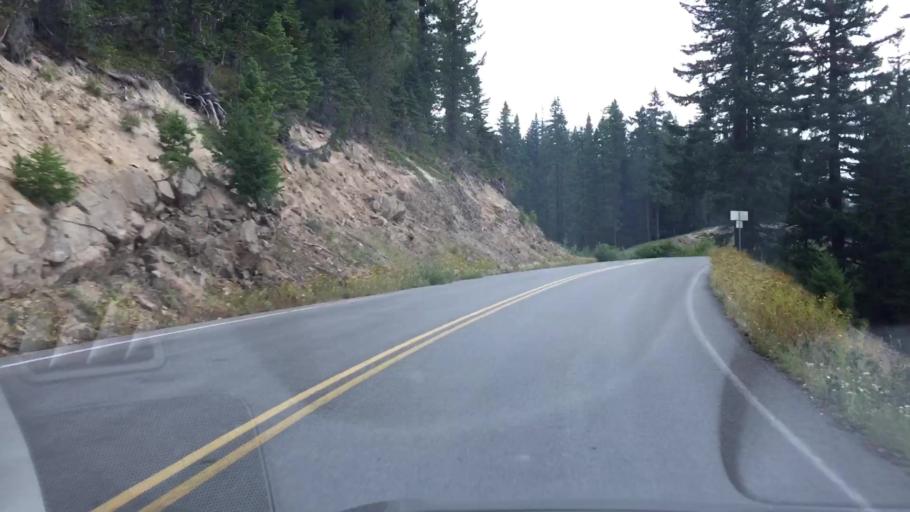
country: US
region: Washington
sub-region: Klickitat County
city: White Salmon
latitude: 46.1584
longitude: -121.6316
